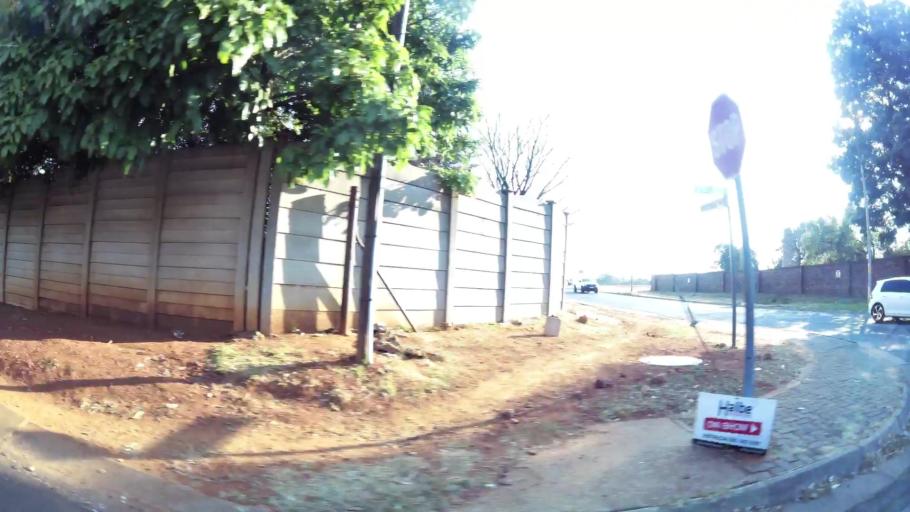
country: ZA
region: Gauteng
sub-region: City of Johannesburg Metropolitan Municipality
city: Modderfontein
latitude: -26.0783
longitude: 28.2047
